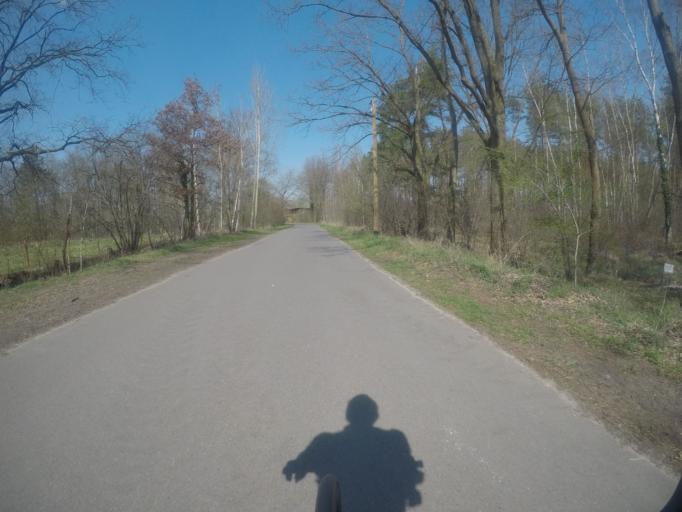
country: DE
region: Brandenburg
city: Falkensee
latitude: 52.6288
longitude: 13.1274
